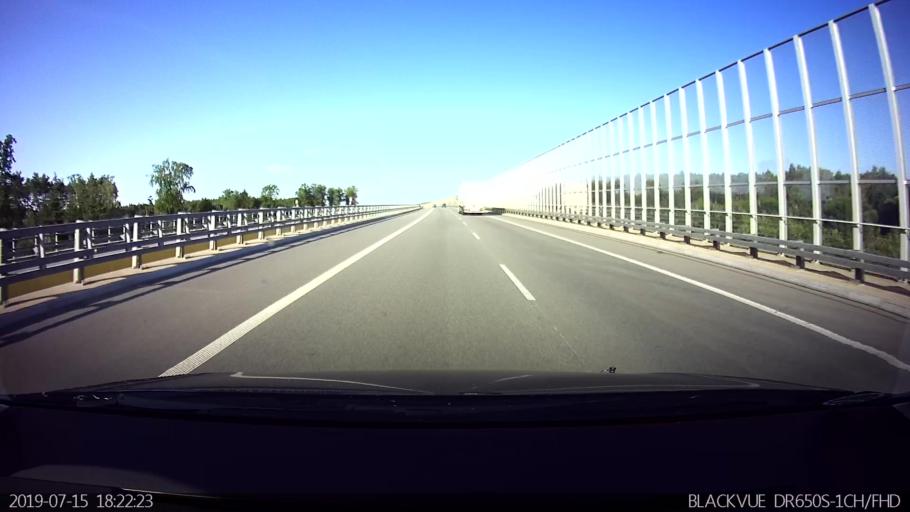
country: PL
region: Lodz Voivodeship
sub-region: Powiat laski
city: Lask
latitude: 51.5543
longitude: 19.1049
